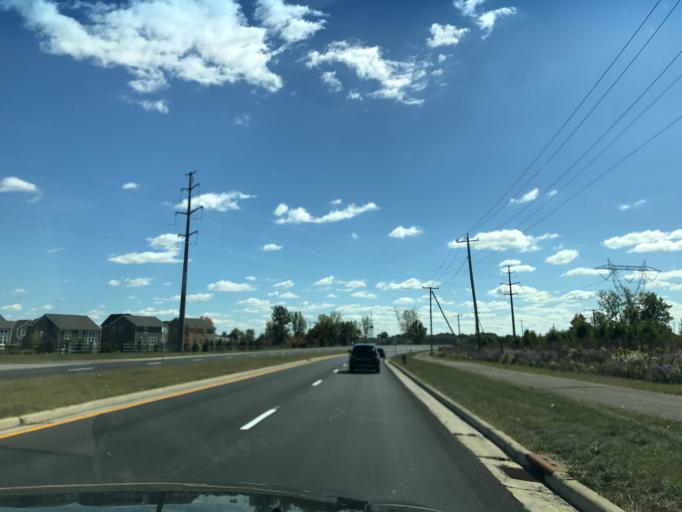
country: US
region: Ohio
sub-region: Delaware County
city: Powell
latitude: 40.2097
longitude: -83.0963
